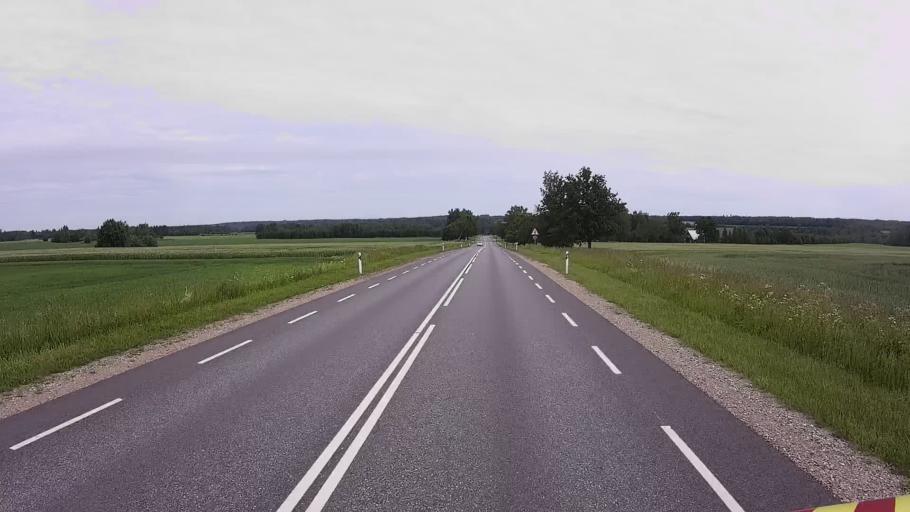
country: EE
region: Viljandimaa
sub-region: Karksi vald
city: Karksi-Nuia
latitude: 58.1364
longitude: 25.5846
